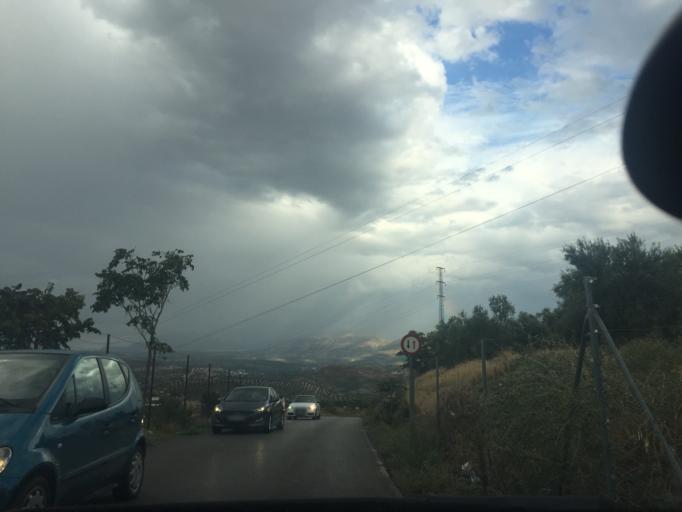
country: ES
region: Andalusia
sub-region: Provincia de Jaen
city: Jaen
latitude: 37.7718
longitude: -3.7797
